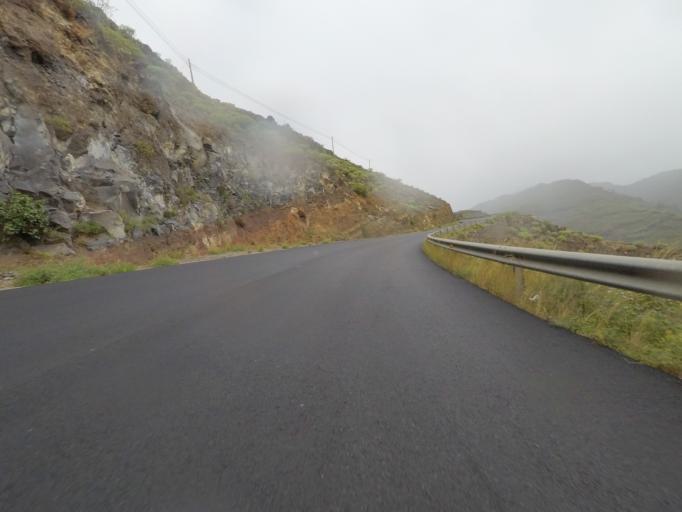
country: ES
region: Canary Islands
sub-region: Provincia de Santa Cruz de Tenerife
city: Alajero
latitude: 28.0559
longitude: -17.2014
